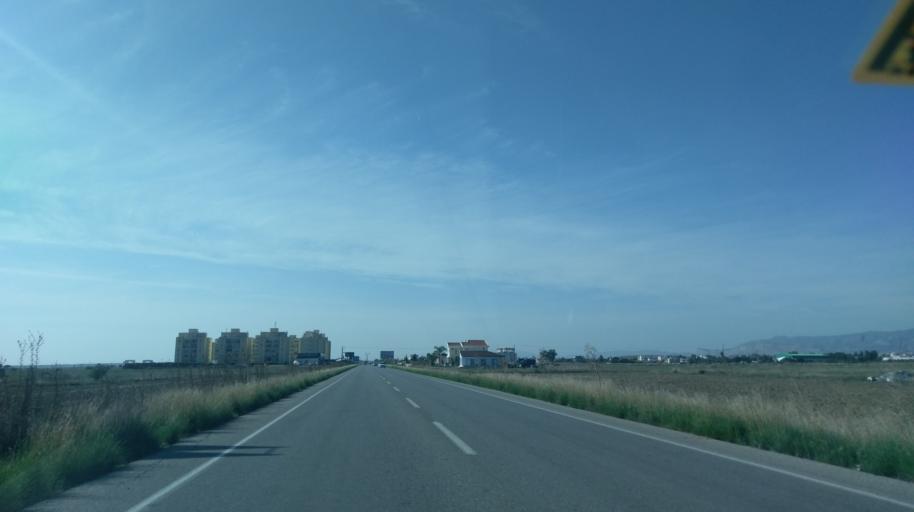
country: CY
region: Ammochostos
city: Trikomo
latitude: 35.2791
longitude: 33.9069
